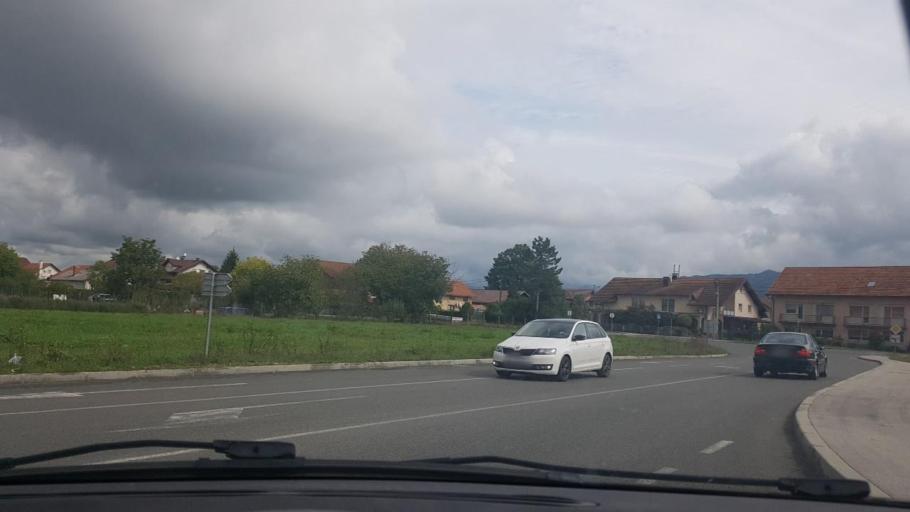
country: HR
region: Zagrebacka
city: Brdovec
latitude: 45.8590
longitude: 15.7889
